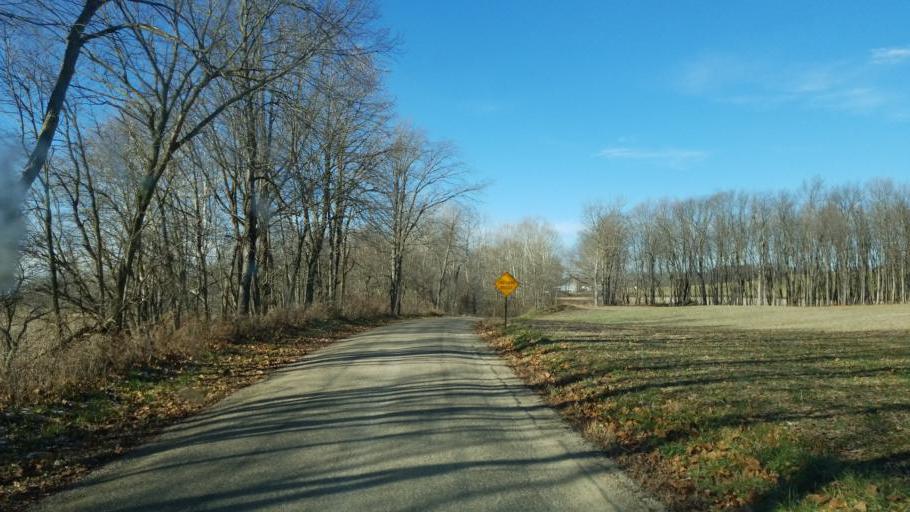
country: US
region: Ohio
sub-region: Richland County
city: Lexington
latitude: 40.6205
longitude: -82.5930
